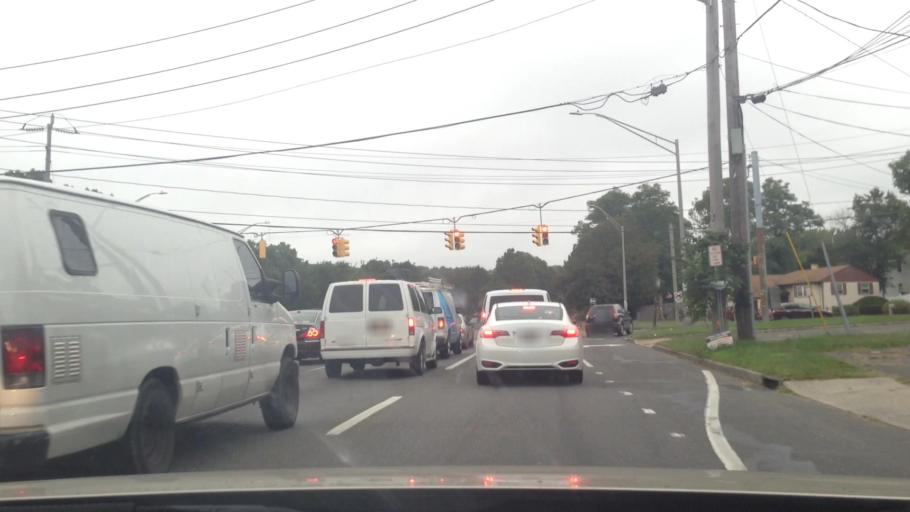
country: US
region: New York
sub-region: Suffolk County
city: Farmingville
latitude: 40.8343
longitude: -73.0212
